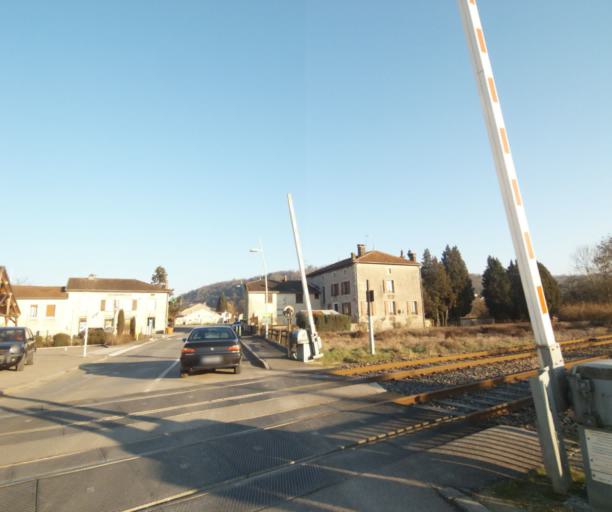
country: FR
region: Champagne-Ardenne
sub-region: Departement de la Haute-Marne
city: Chevillon
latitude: 48.5239
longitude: 5.1119
